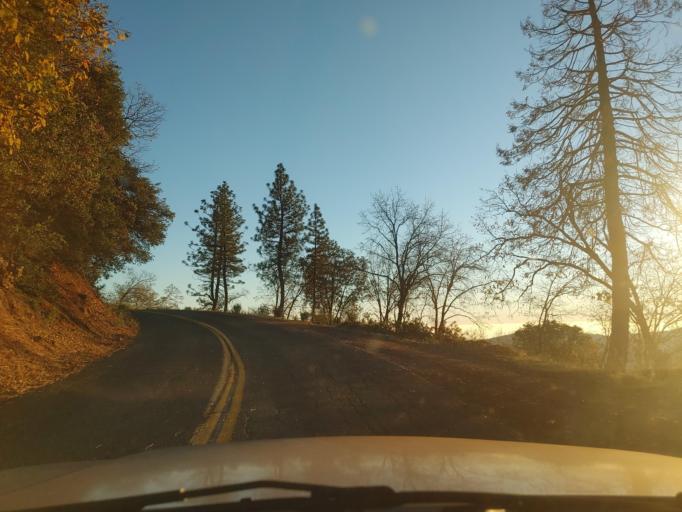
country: US
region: California
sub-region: Tuolumne County
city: Cedar Ridge
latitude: 38.0378
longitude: -120.3103
